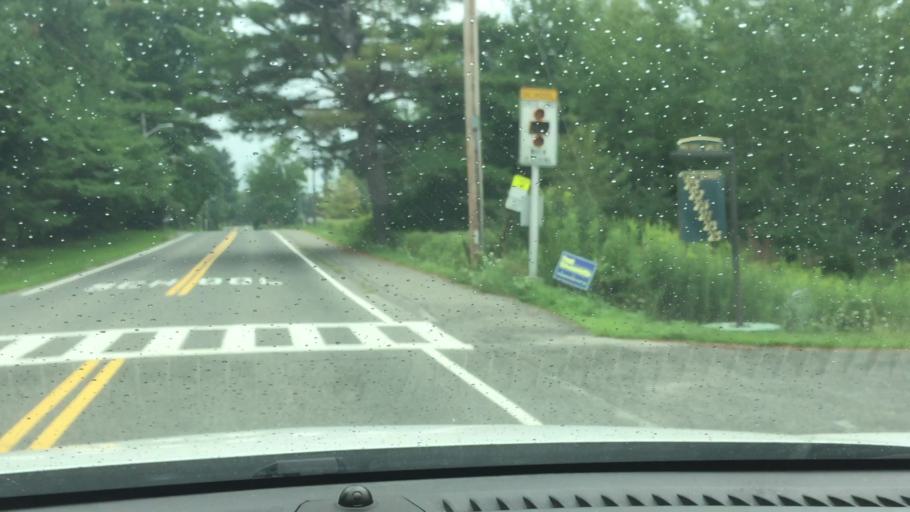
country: US
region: Massachusetts
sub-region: Berkshire County
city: Lenox
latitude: 42.3534
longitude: -73.2585
